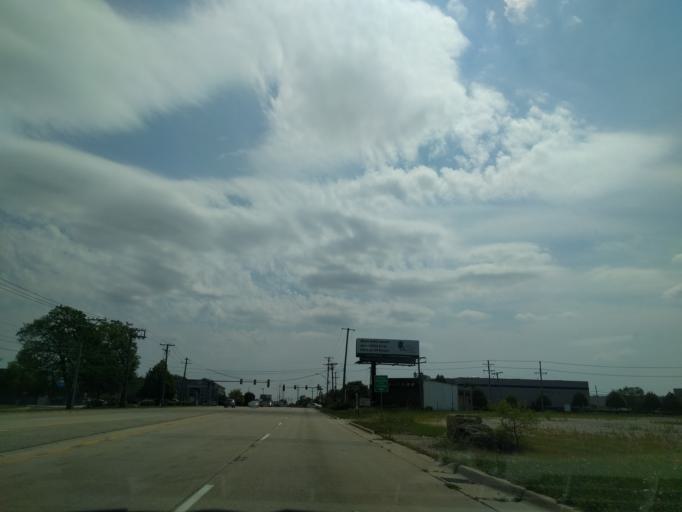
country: US
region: Illinois
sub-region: Cook County
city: Elk Grove Village
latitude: 42.0115
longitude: -87.9457
